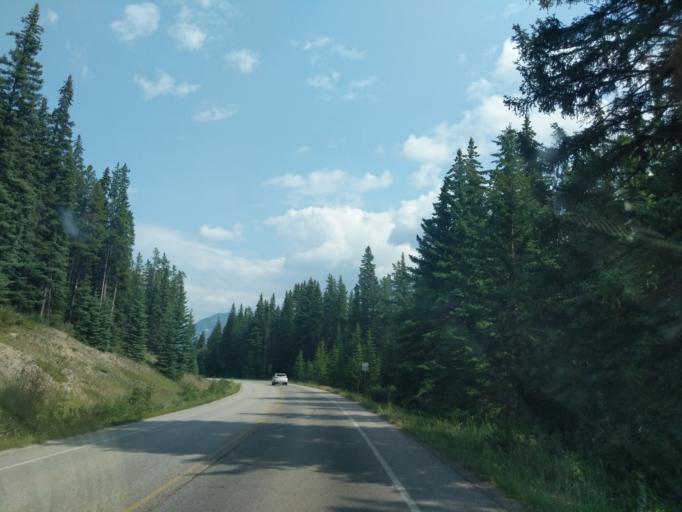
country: CA
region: Alberta
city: Banff
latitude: 51.1684
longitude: -115.6938
